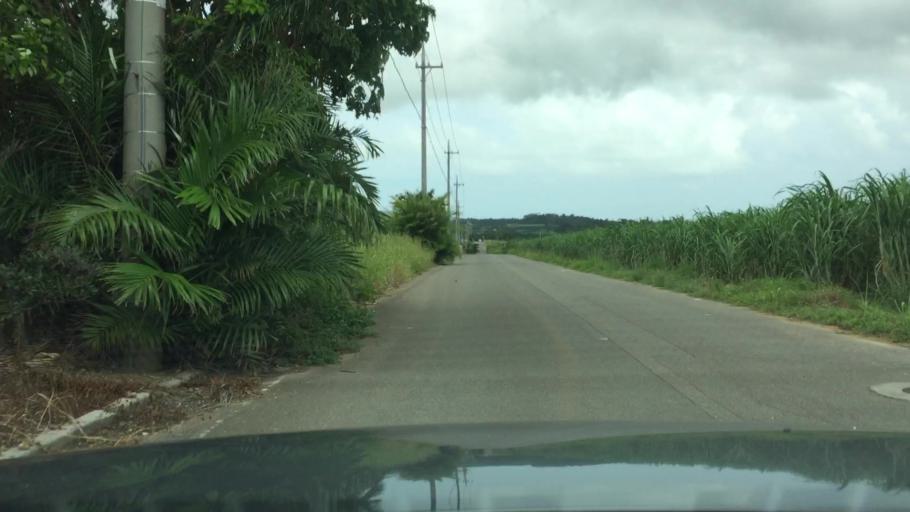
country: JP
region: Okinawa
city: Ishigaki
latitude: 24.3969
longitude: 124.1886
